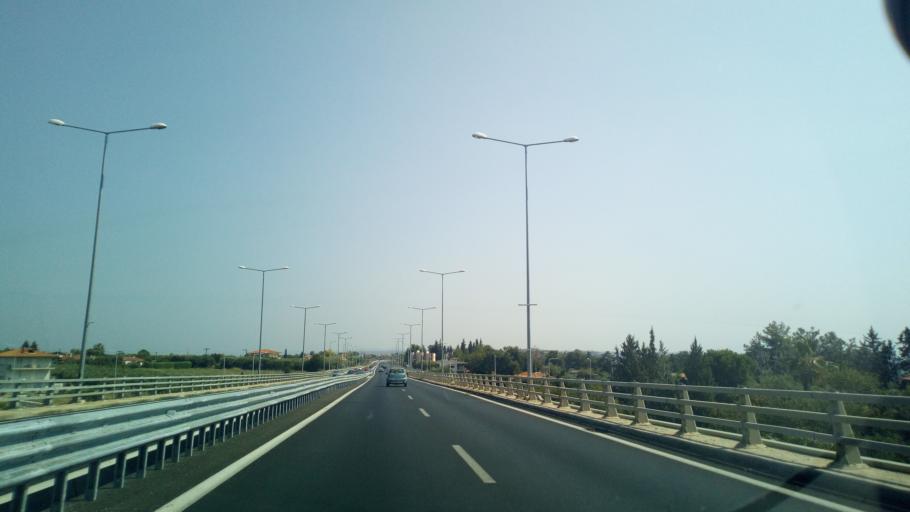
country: GR
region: Central Macedonia
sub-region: Nomos Chalkidikis
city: Nea Moudhania
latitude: 40.2262
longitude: 23.3129
